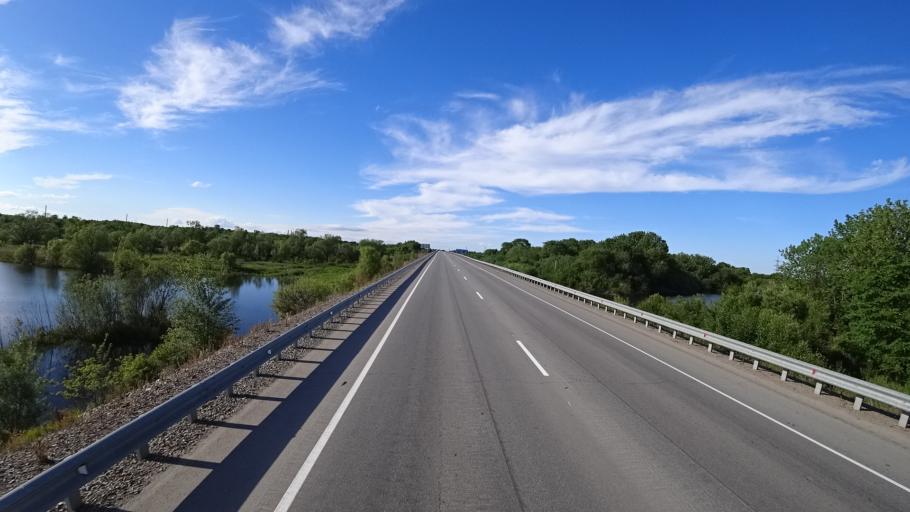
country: RU
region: Khabarovsk Krai
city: Khor
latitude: 47.8594
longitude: 134.9627
